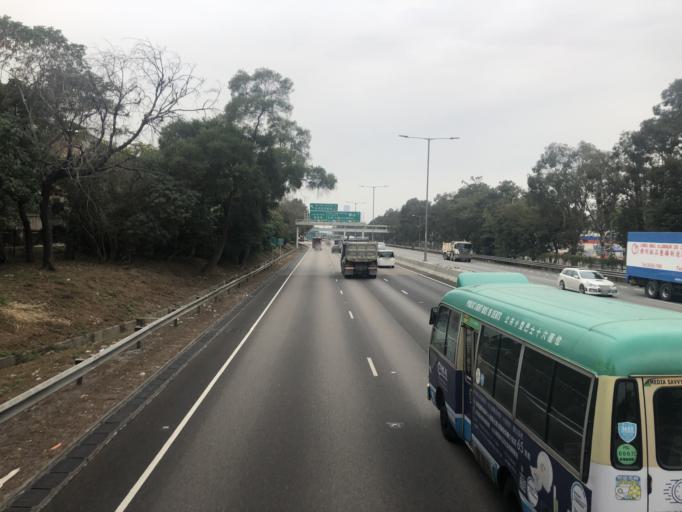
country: CN
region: Guangdong
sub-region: Shenzhen
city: Shenzhen
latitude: 22.5036
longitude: 114.0974
